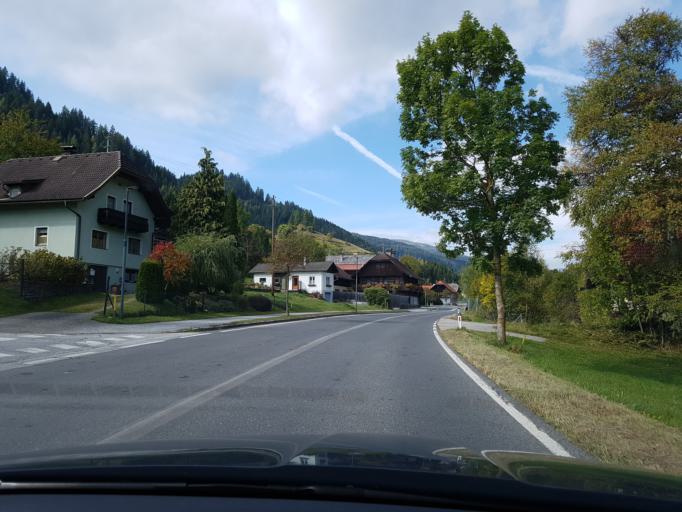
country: AT
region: Carinthia
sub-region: Politischer Bezirk Feldkirchen
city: Gnesau
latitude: 46.7764
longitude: 13.9583
